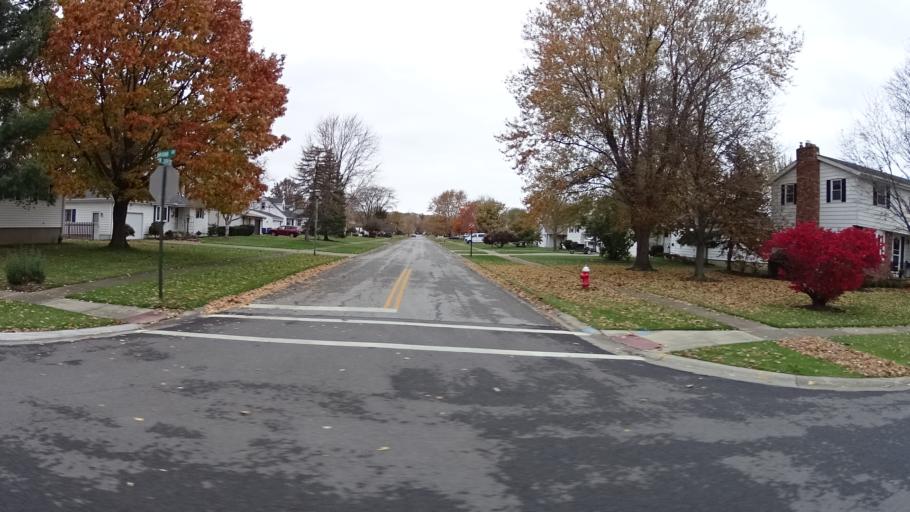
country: US
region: Ohio
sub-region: Lorain County
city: Lorain
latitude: 41.4362
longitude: -82.2037
